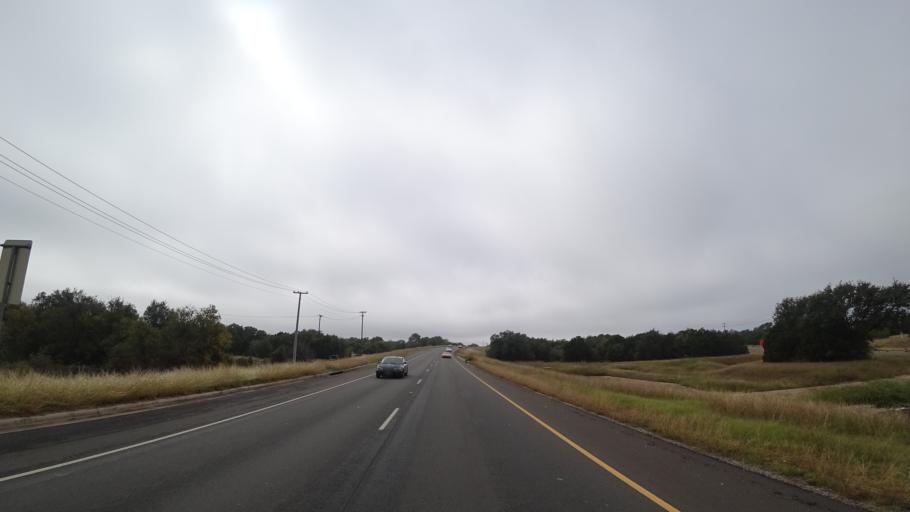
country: US
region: Texas
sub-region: Travis County
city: Shady Hollow
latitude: 30.1828
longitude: -97.8798
